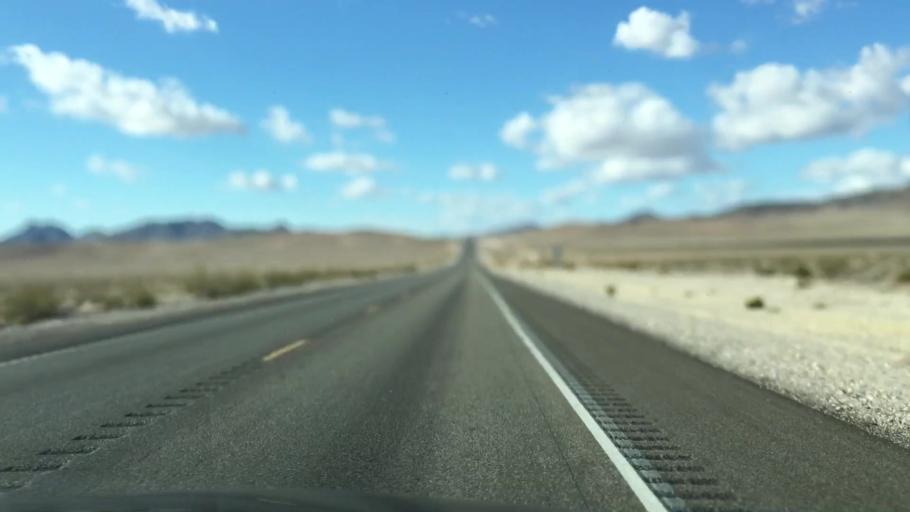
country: US
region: Nevada
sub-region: Nye County
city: Pahrump
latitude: 36.6059
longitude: -116.2597
